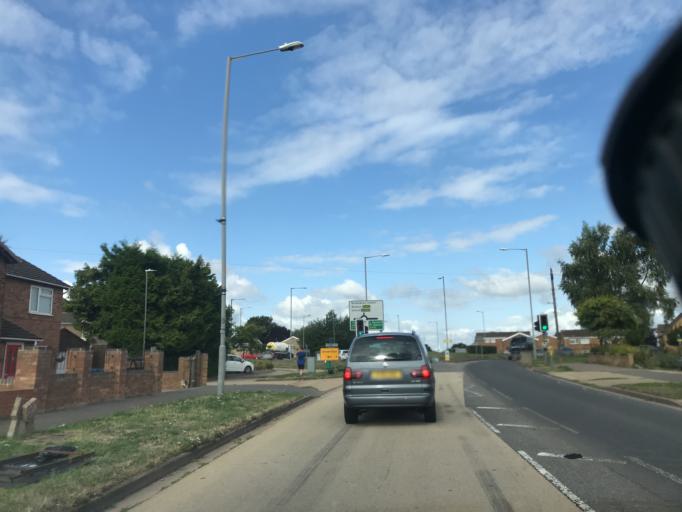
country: GB
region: England
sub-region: Buckinghamshire
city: Aylesbury
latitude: 51.8235
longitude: -0.7978
